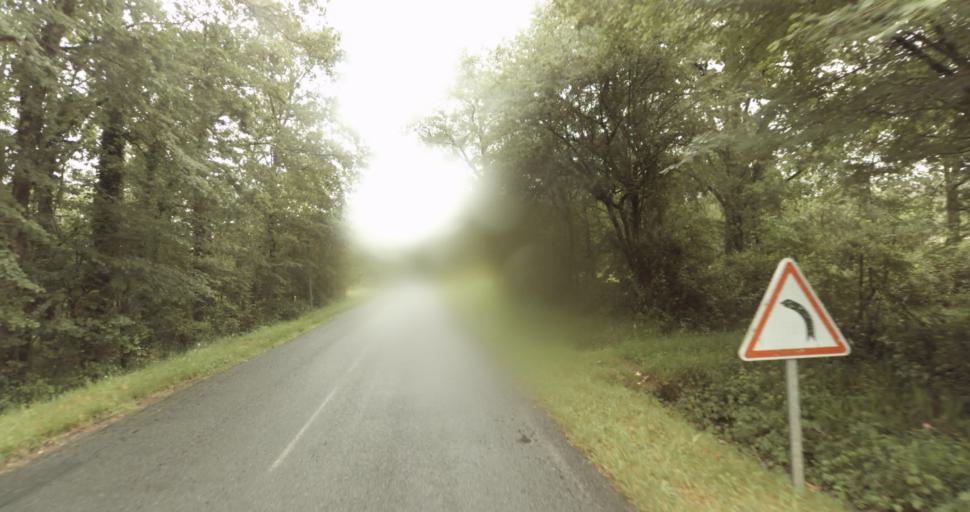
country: FR
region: Aquitaine
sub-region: Departement de la Dordogne
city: Beaumont-du-Perigord
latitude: 44.8012
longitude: 0.8512
